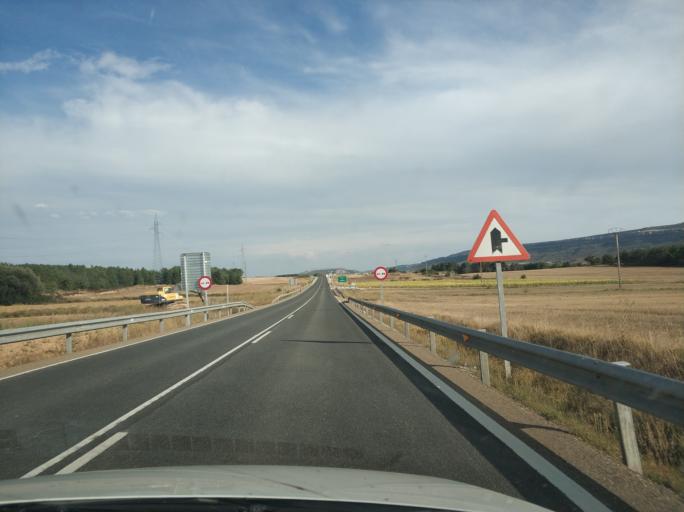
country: ES
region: Castille and Leon
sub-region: Provincia de Palencia
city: Pomar de Valdivia
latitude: 42.7478
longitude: -4.1637
